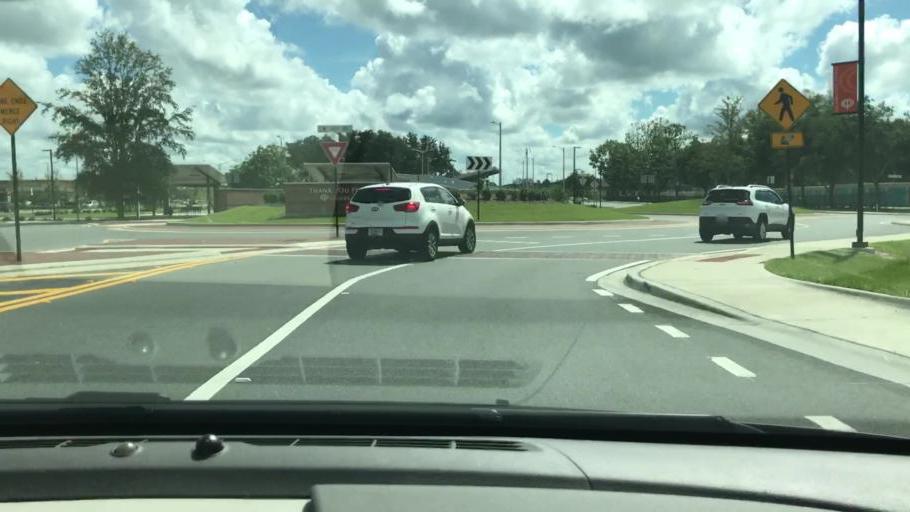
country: US
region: Florida
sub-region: Alachua County
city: Gainesville
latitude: 29.6253
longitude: -82.3891
